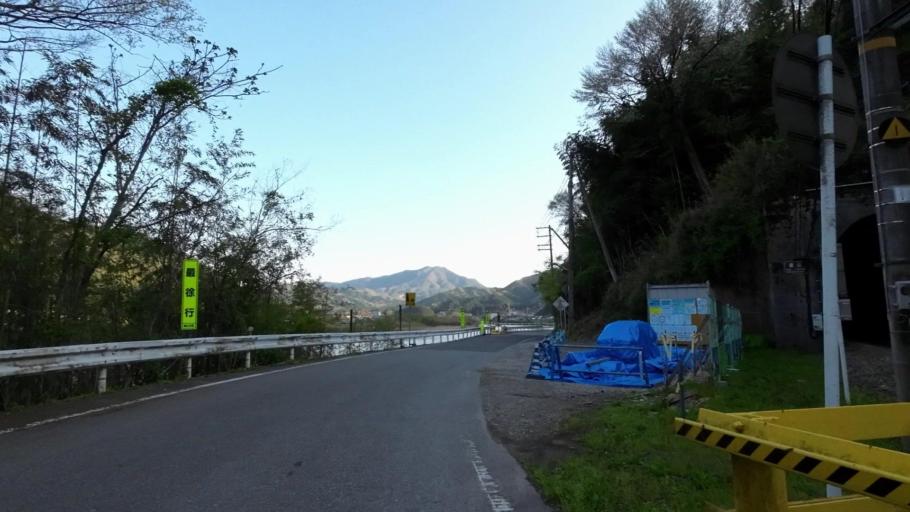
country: JP
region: Hyogo
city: Toyooka
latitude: 35.3807
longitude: 134.8133
